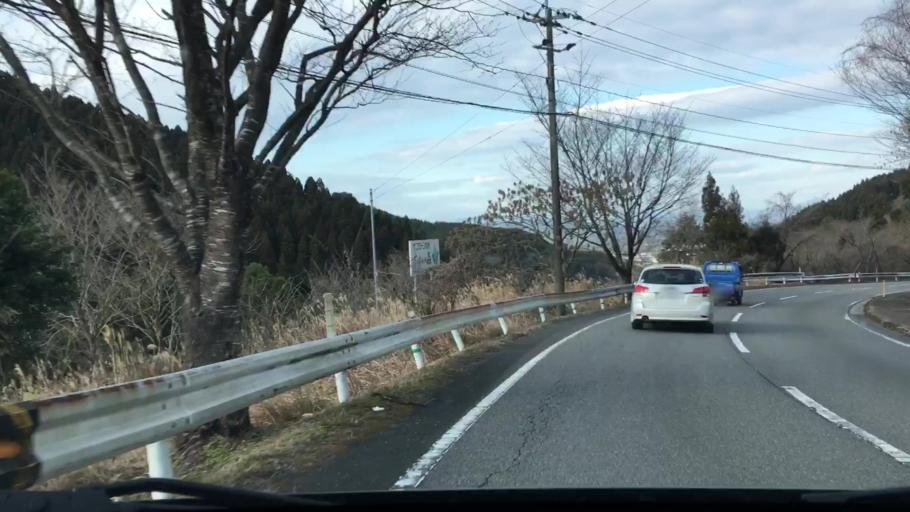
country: JP
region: Miyazaki
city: Miyazaki-shi
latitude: 31.8042
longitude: 131.3013
